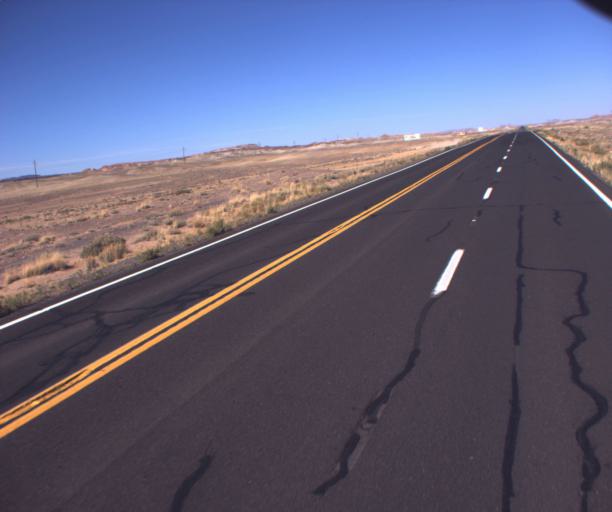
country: US
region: Arizona
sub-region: Coconino County
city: Tuba City
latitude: 35.9444
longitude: -111.3994
